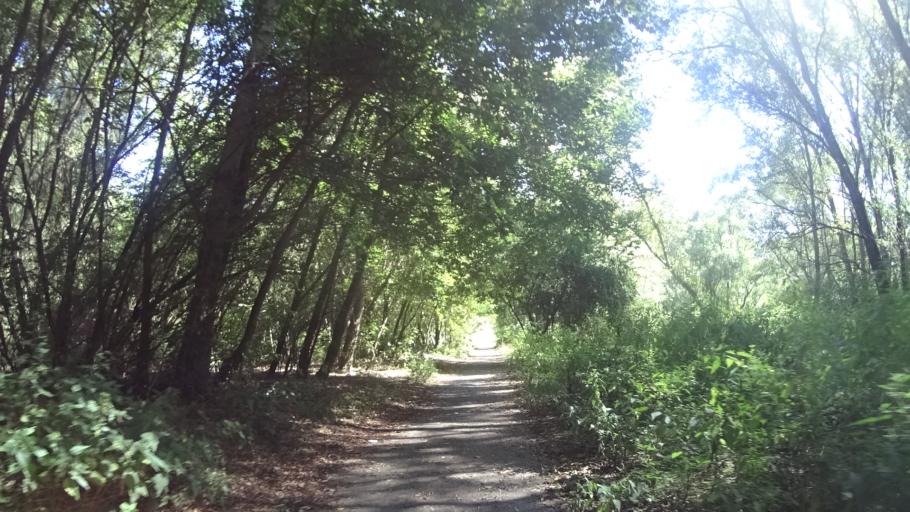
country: AT
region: Lower Austria
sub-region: Politischer Bezirk Bruck an der Leitha
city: Hainburg an der Donau
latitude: 48.1793
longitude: 16.9777
